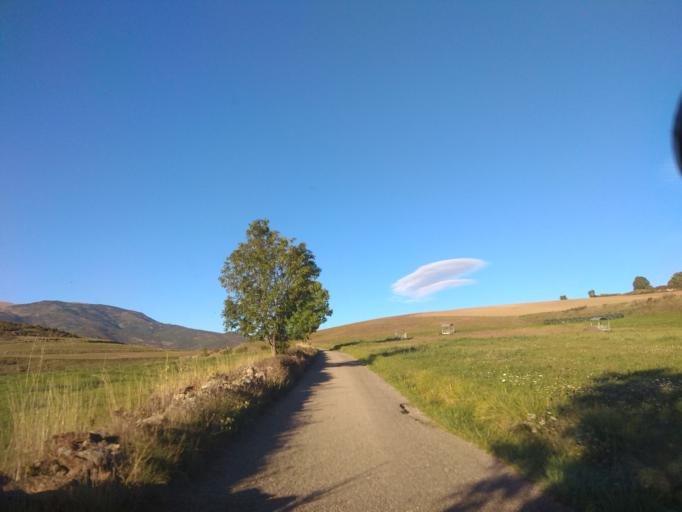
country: ES
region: Catalonia
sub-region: Provincia de Lleida
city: Lles de Cerdanya
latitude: 42.3520
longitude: 1.7098
